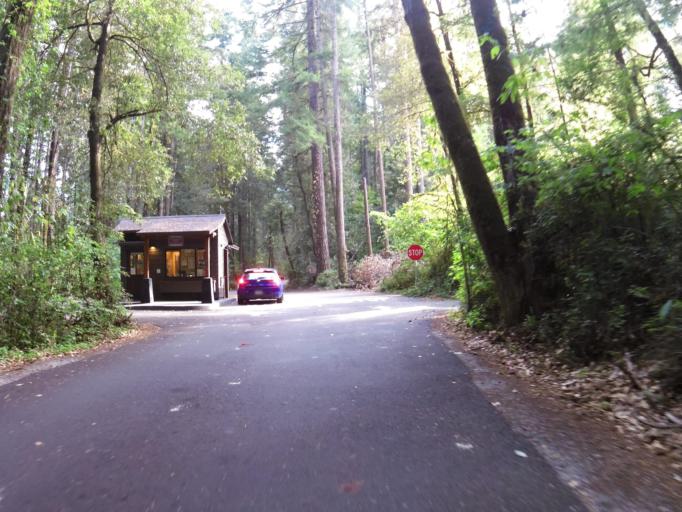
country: US
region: California
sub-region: Del Norte County
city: Bertsch-Oceanview
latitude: 41.7974
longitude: -124.0856
